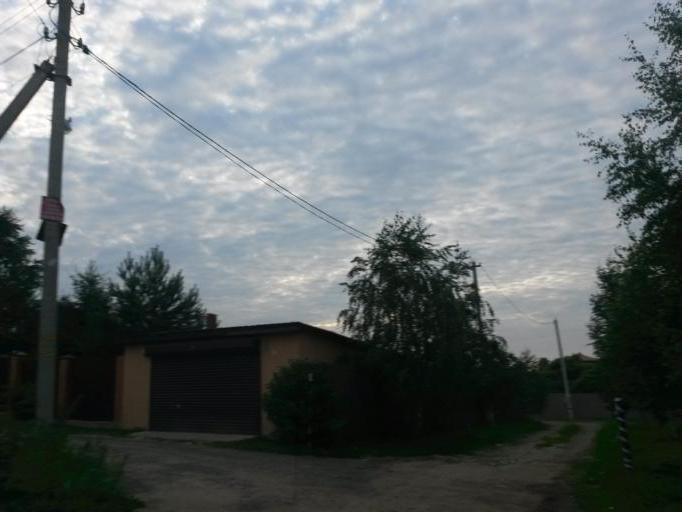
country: RU
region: Moskovskaya
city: Lyubuchany
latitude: 55.2558
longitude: 37.6115
